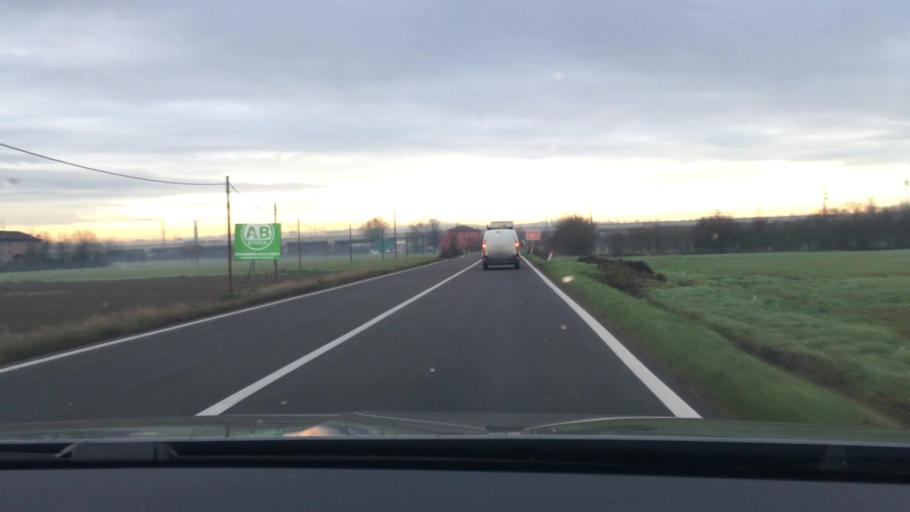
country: IT
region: Emilia-Romagna
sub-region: Provincia di Modena
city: Albareto
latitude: 44.6957
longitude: 10.9464
